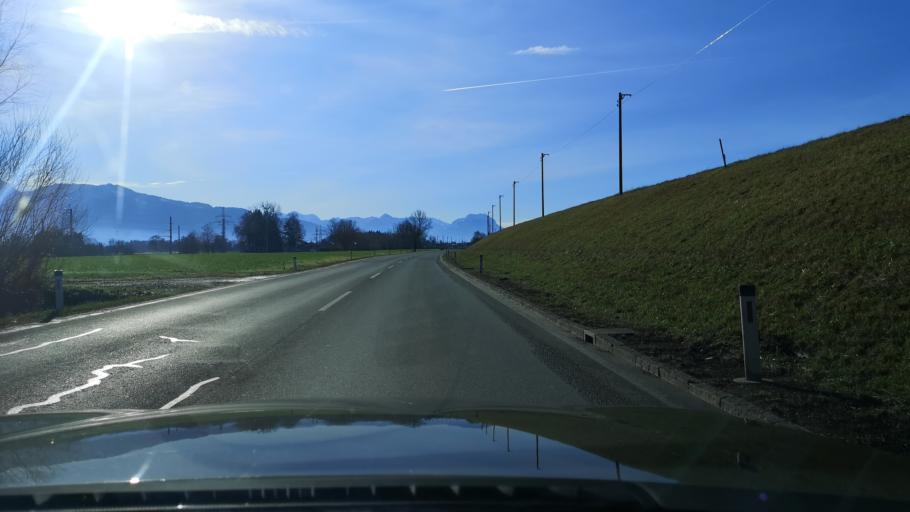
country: AT
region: Vorarlberg
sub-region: Politischer Bezirk Bregenz
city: Fussach
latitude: 47.4597
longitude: 9.6702
